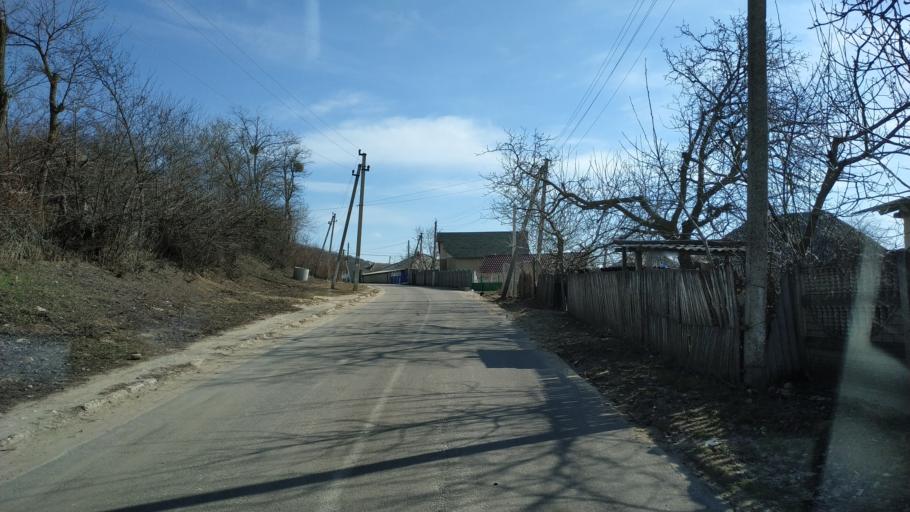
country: MD
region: Nisporeni
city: Nisporeni
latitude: 47.2214
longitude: 28.0486
